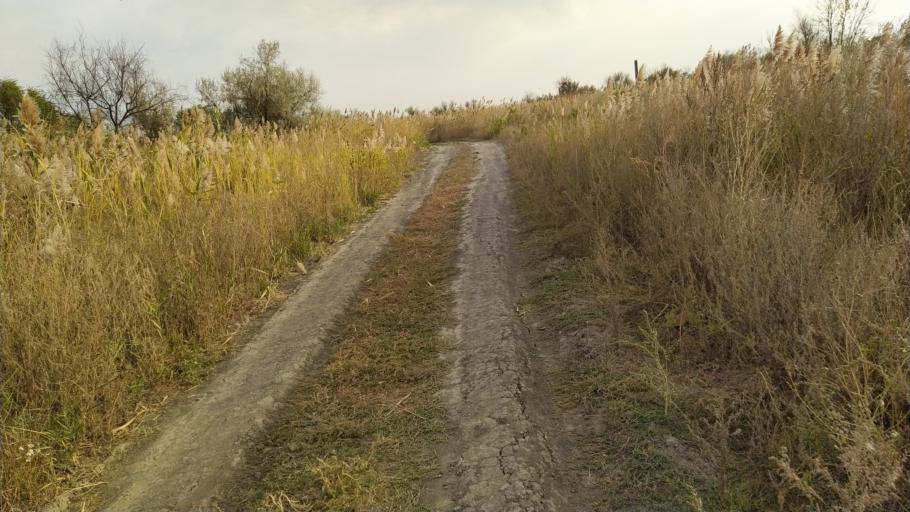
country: RU
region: Rostov
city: Kuleshovka
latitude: 47.1220
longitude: 39.6011
